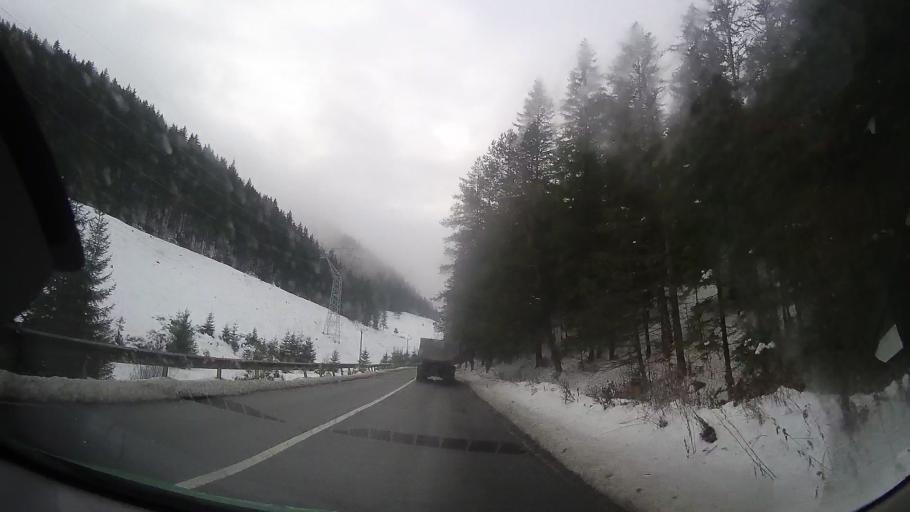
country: RO
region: Neamt
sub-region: Comuna Bicaz Chei
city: Bicaz Chei
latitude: 46.7781
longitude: 25.7647
